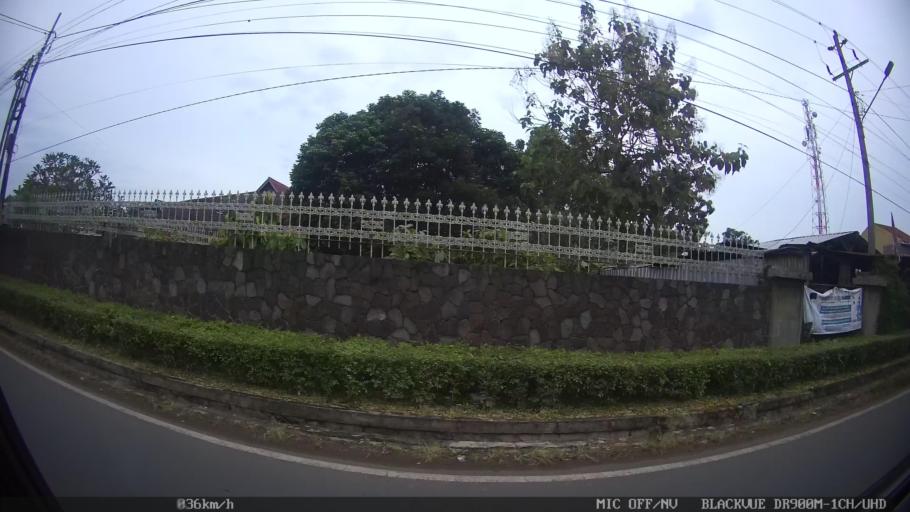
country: ID
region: Lampung
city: Kedaton
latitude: -5.3919
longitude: 105.2338
